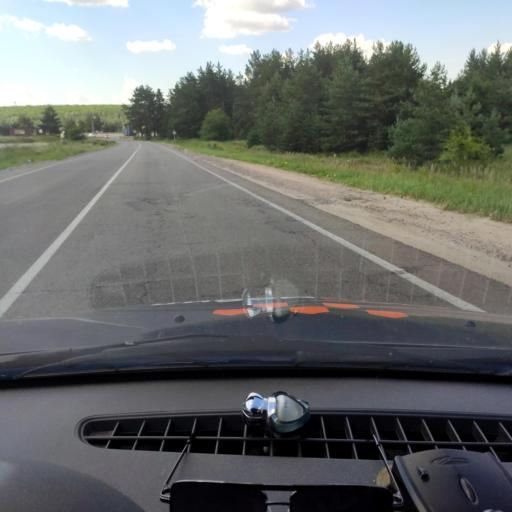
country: RU
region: Voronezj
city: Novovoronezh
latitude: 51.3291
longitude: 39.2556
